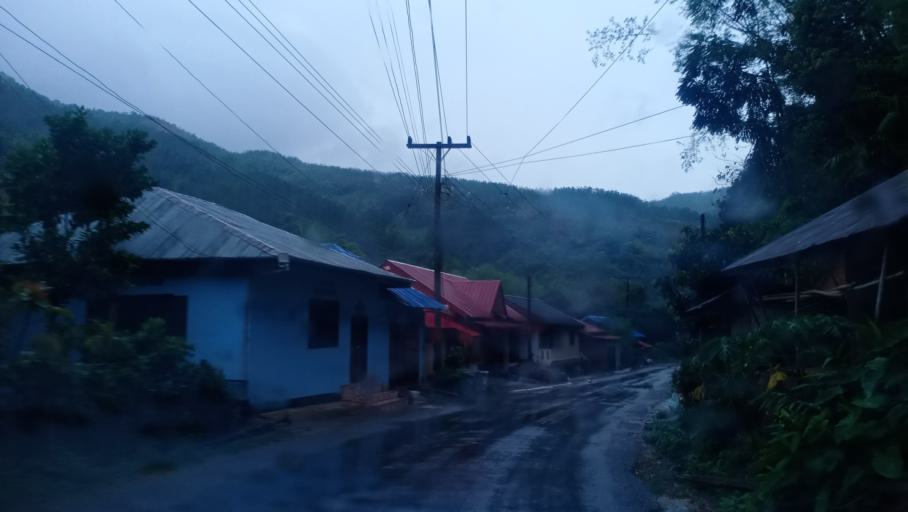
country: LA
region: Phongsali
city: Khoa
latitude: 21.0740
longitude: 102.5033
